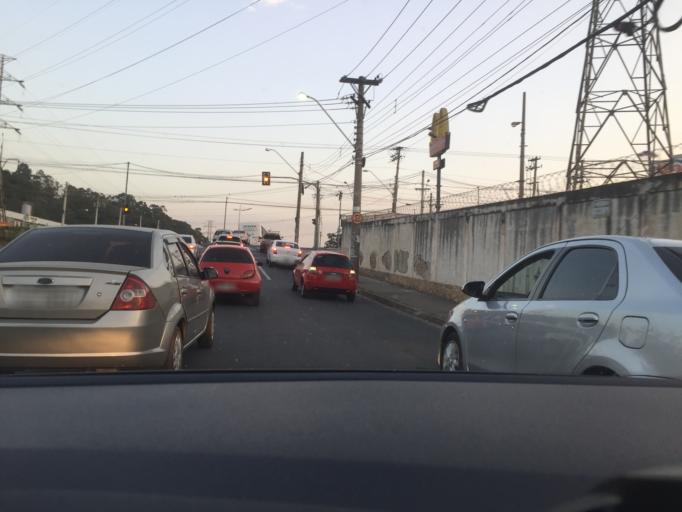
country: BR
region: Sao Paulo
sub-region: Varzea Paulista
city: Varzea Paulista
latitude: -23.2124
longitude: -46.8398
